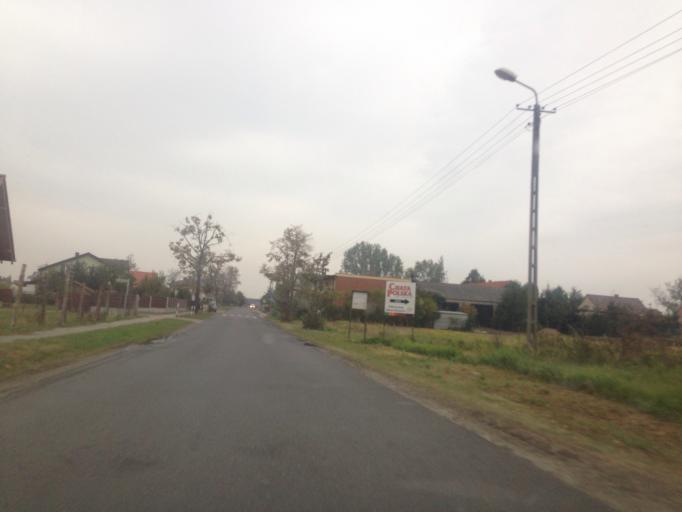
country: PL
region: Greater Poland Voivodeship
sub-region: Powiat poznanski
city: Kleszczewo
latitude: 52.3633
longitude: 17.1283
